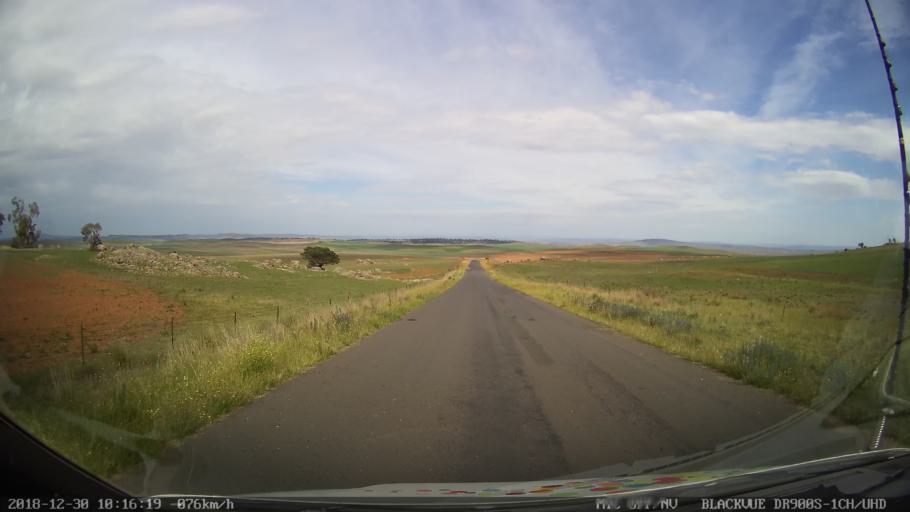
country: AU
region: New South Wales
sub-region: Snowy River
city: Berridale
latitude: -36.5472
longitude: 149.0364
